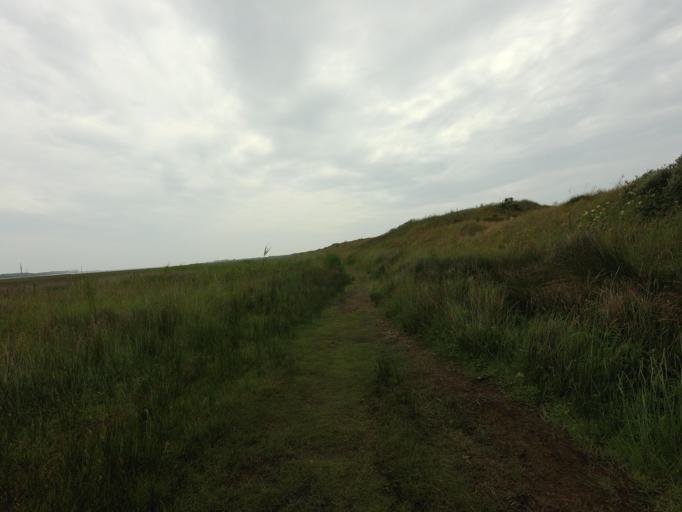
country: NL
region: North Holland
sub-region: Gemeente Den Helder
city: Den Helder
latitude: 53.0109
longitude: 4.7443
